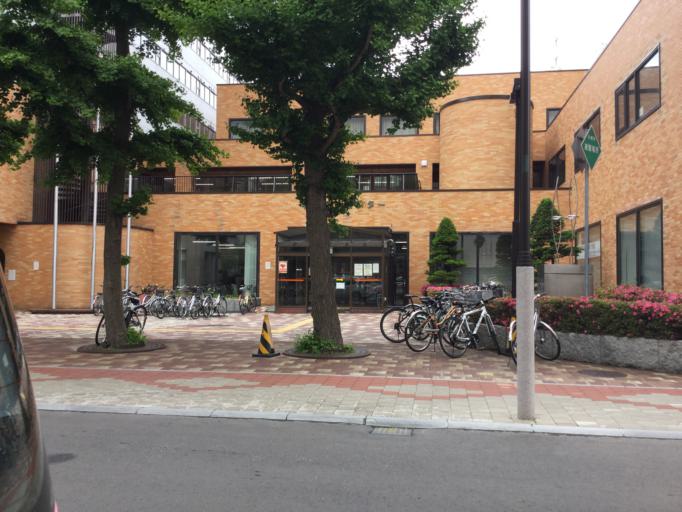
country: JP
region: Hokkaido
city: Sapporo
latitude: 43.0560
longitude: 141.3425
